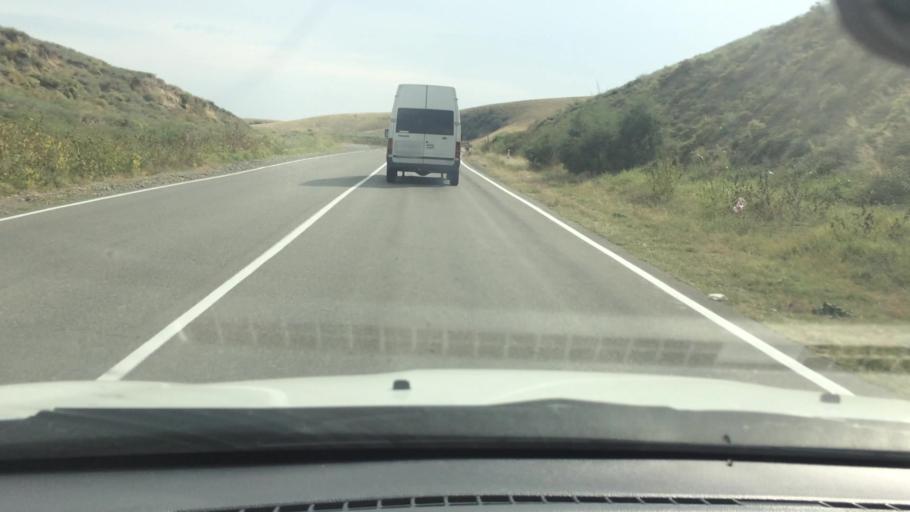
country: GE
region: Kvemo Kartli
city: Rust'avi
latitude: 41.5228
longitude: 44.9884
